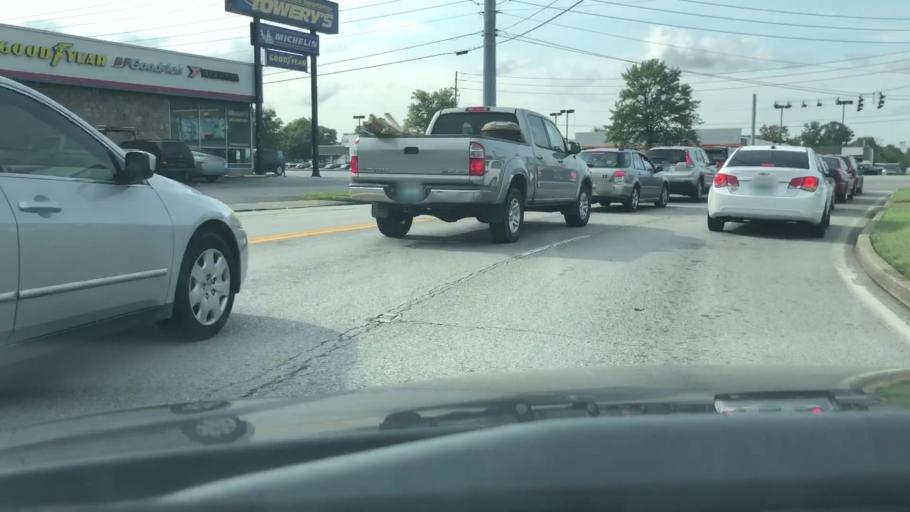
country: US
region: Kentucky
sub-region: Jefferson County
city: Lyndon
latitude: 38.2502
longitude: -85.6151
